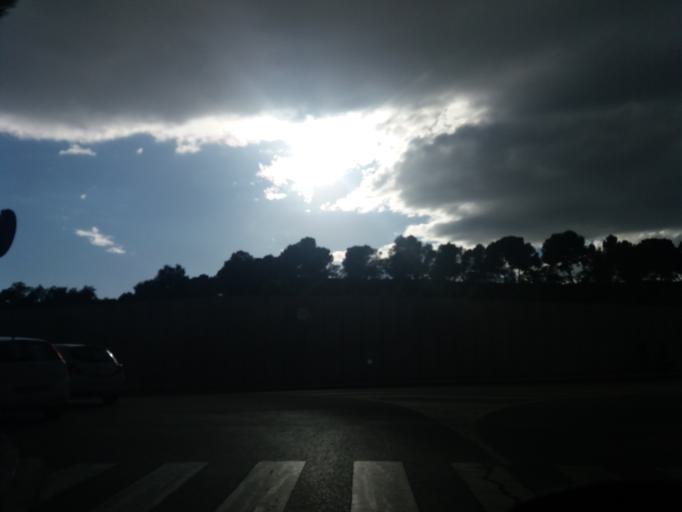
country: ES
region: Catalonia
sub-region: Provincia de Barcelona
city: Manresa
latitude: 41.7414
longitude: 1.8341
